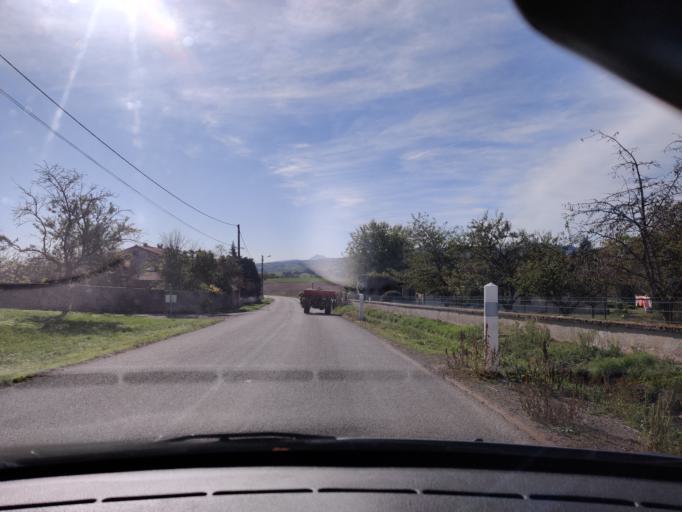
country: FR
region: Auvergne
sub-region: Departement du Puy-de-Dome
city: Combronde
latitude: 46.0207
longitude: 3.0969
